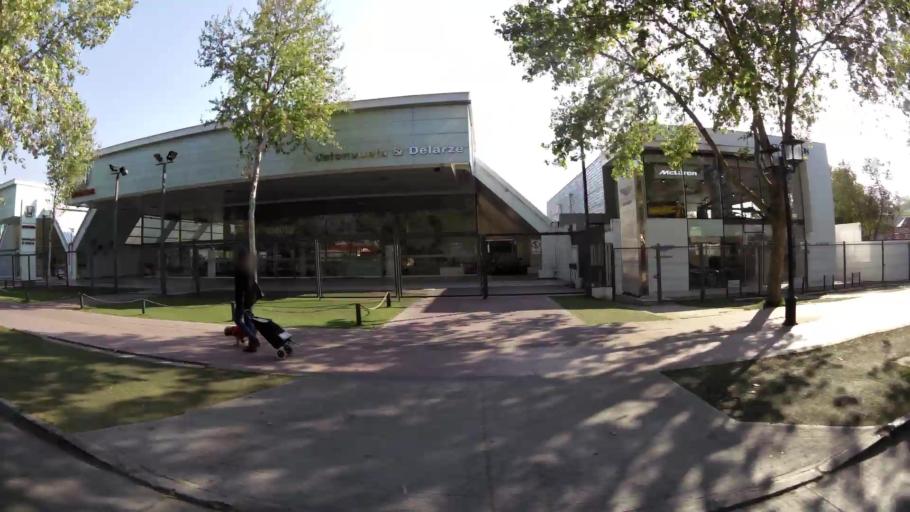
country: CL
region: Santiago Metropolitan
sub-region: Provincia de Santiago
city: Villa Presidente Frei, Nunoa, Santiago, Chile
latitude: -33.3847
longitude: -70.5508
